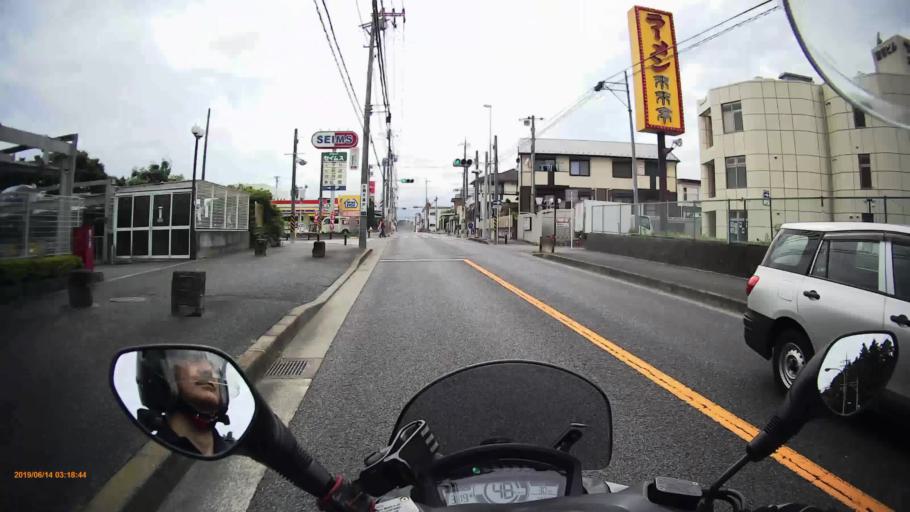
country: JP
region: Kanagawa
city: Minami-rinkan
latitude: 35.4196
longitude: 139.4537
